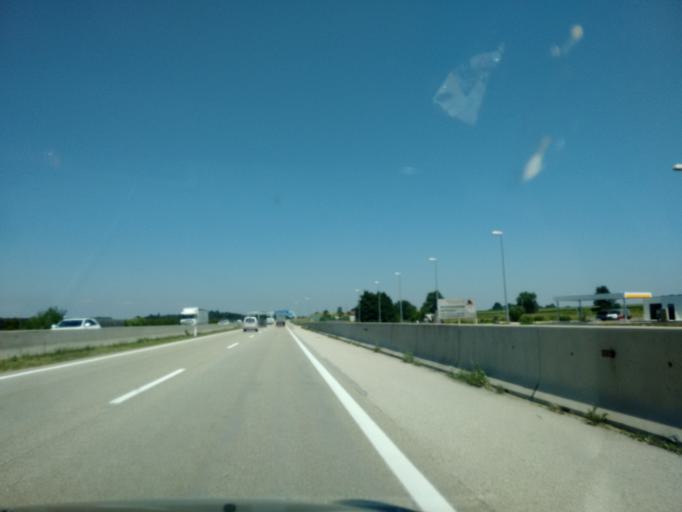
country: AT
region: Upper Austria
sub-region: Wels-Land
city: Sattledt
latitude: 48.0408
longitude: 13.9915
